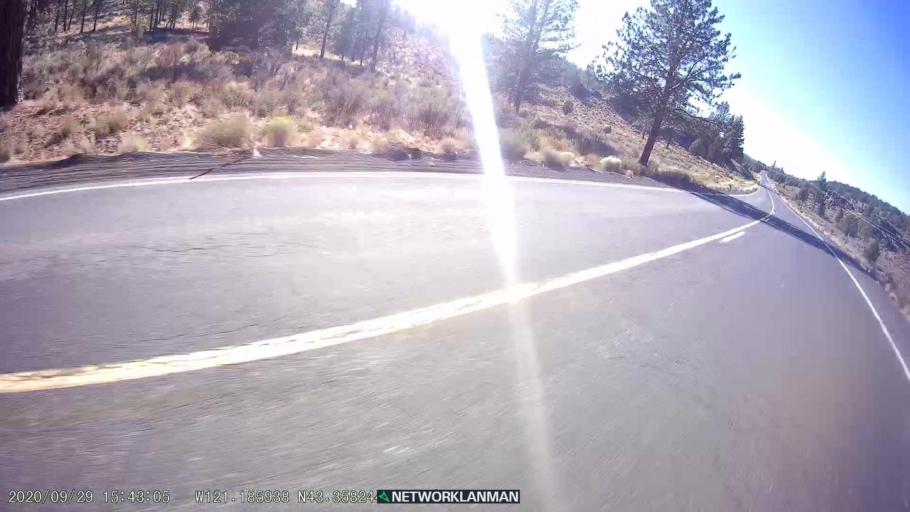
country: US
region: Oregon
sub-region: Deschutes County
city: La Pine
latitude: 43.3583
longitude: -121.1861
